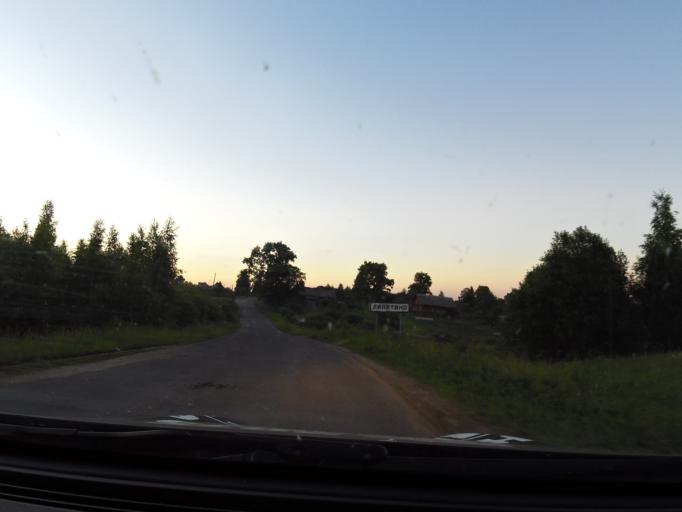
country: RU
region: Kostroma
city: Buy
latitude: 58.4009
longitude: 41.2386
